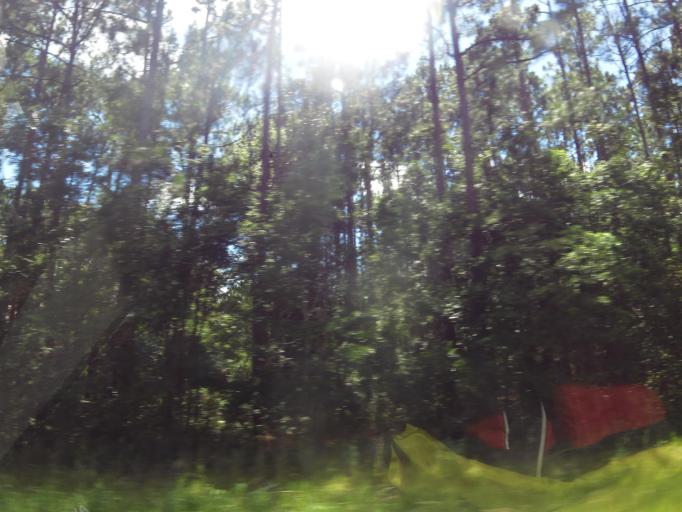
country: US
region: Georgia
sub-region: Camden County
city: St. Marys
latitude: 30.6602
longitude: -81.5357
